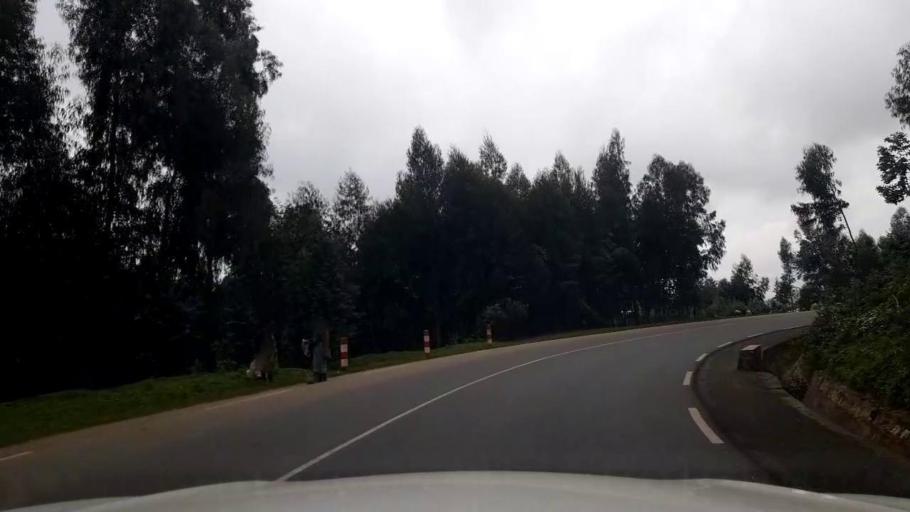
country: RW
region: Northern Province
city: Musanze
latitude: -1.6454
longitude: 29.5037
